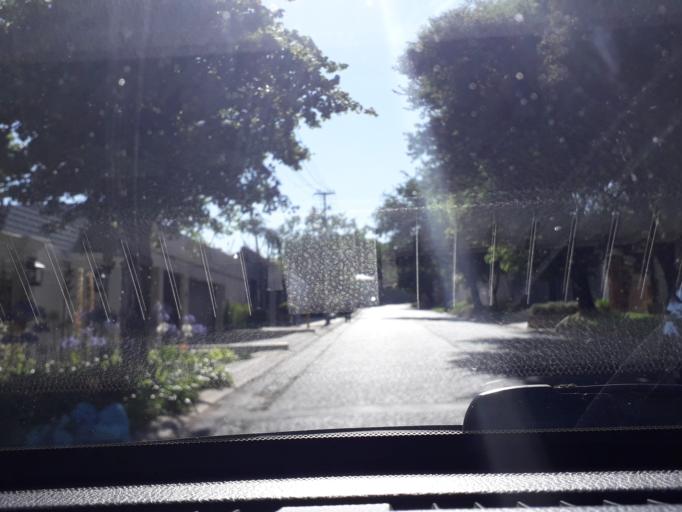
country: ZA
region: Gauteng
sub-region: City of Johannesburg Metropolitan Municipality
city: Johannesburg
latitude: -26.1341
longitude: 28.0233
